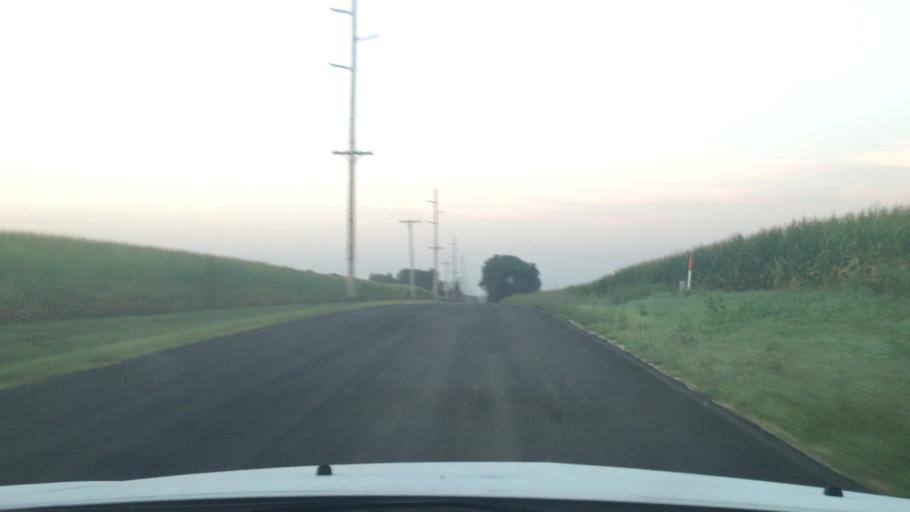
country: US
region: Illinois
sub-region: Ogle County
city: Rochelle
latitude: 41.9170
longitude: -89.0001
